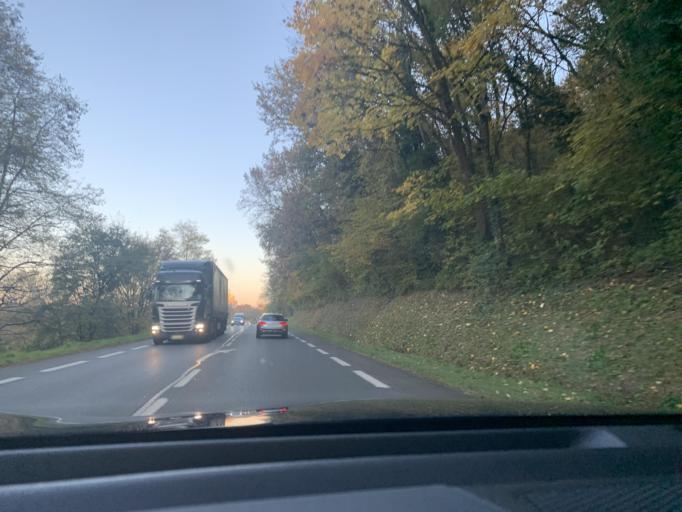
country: FR
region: Rhone-Alpes
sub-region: Departement du Rhone
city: Limas
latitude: 45.9792
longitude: 4.6868
